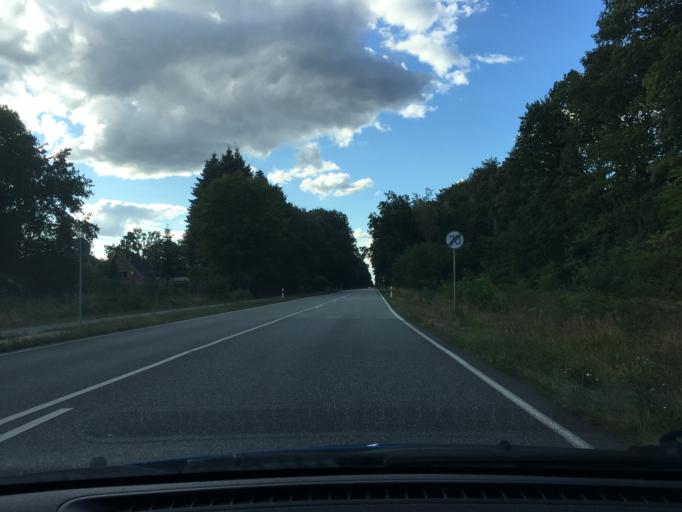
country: DE
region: Mecklenburg-Vorpommern
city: Ludwigslust
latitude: 53.3056
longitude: 11.5225
